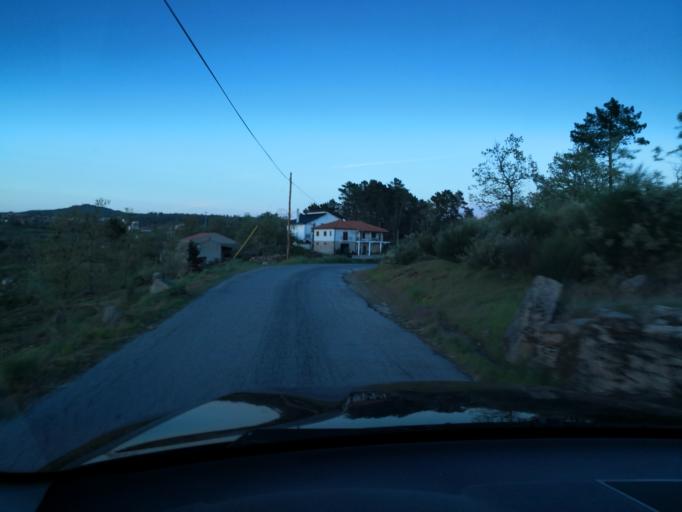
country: PT
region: Vila Real
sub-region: Vila Real
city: Vila Real
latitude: 41.3524
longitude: -7.6773
